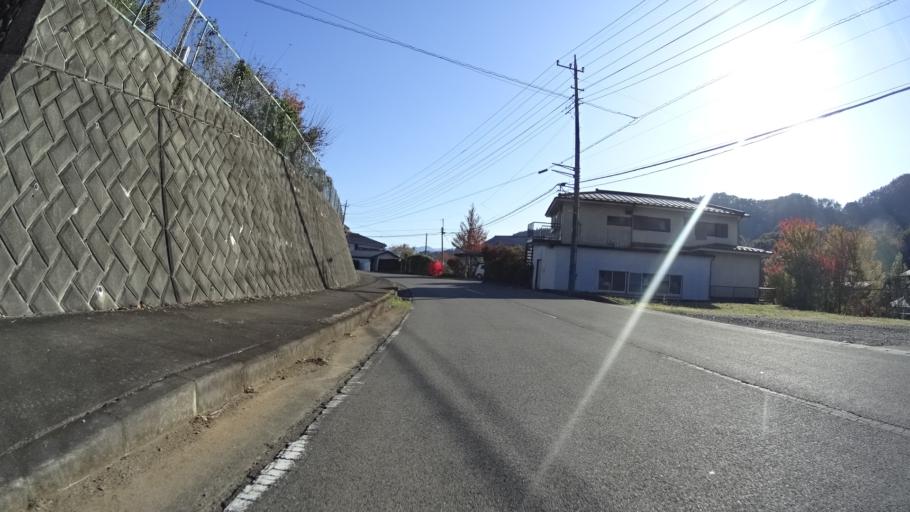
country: JP
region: Yamanashi
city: Uenohara
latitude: 35.6533
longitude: 139.1202
